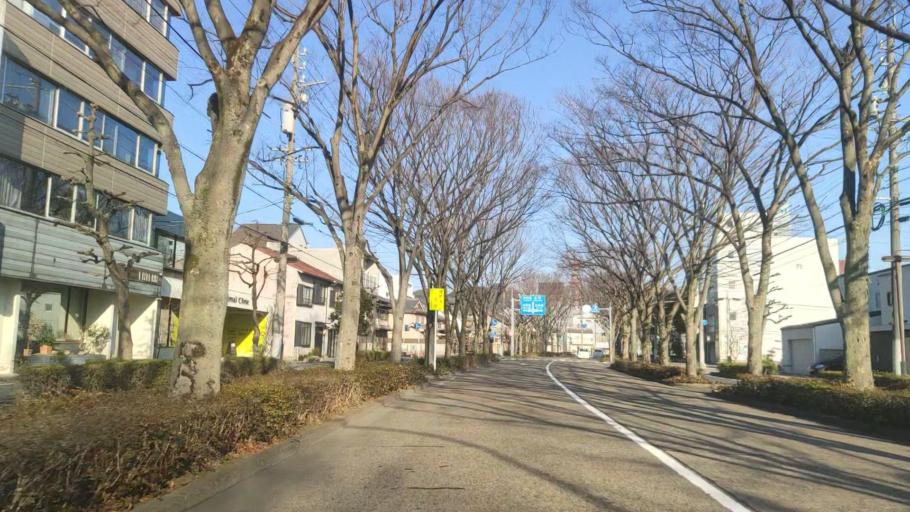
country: JP
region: Gifu
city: Gifu-shi
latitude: 35.4213
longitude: 136.7500
